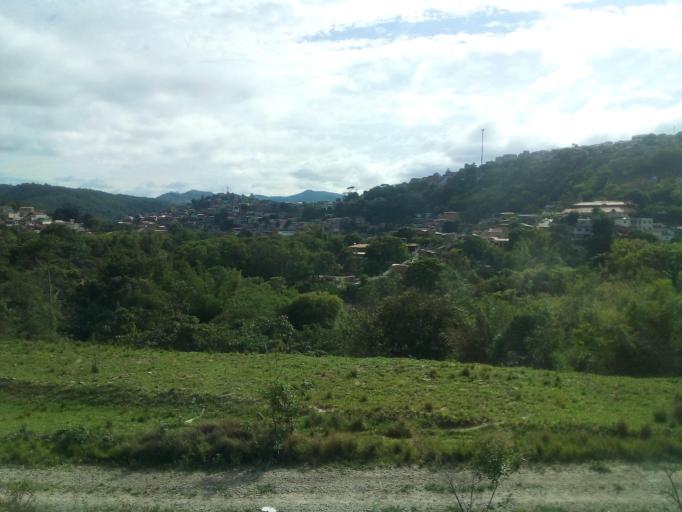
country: BR
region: Minas Gerais
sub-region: Belo Horizonte
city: Belo Horizonte
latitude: -19.8868
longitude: -43.8638
